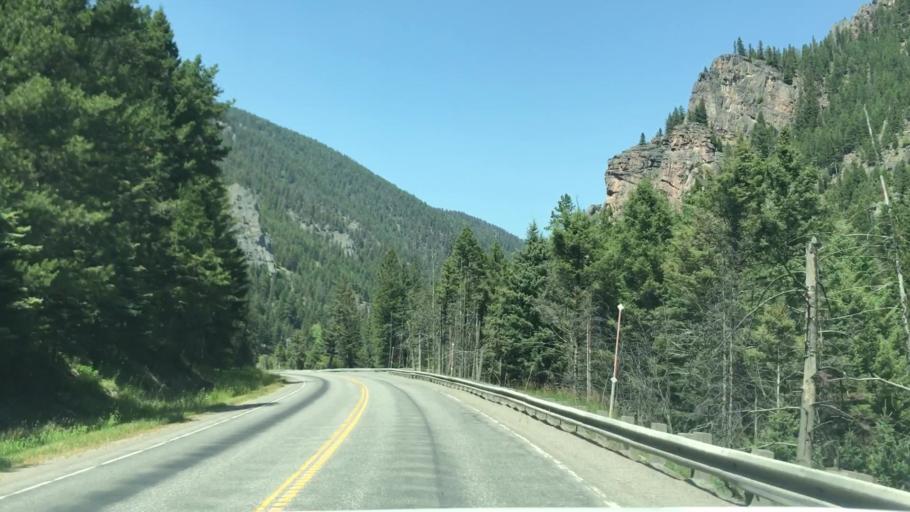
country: US
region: Montana
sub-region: Gallatin County
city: Big Sky
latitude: 45.4122
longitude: -111.2285
